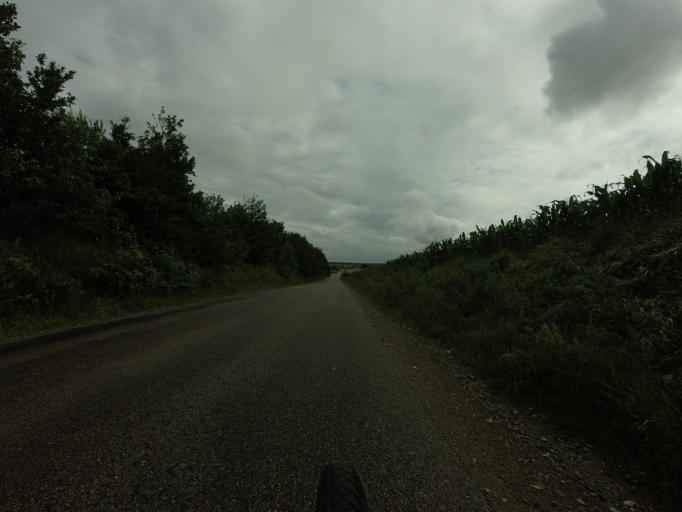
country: DK
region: North Denmark
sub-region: Jammerbugt Kommune
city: Pandrup
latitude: 57.3119
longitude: 9.7287
